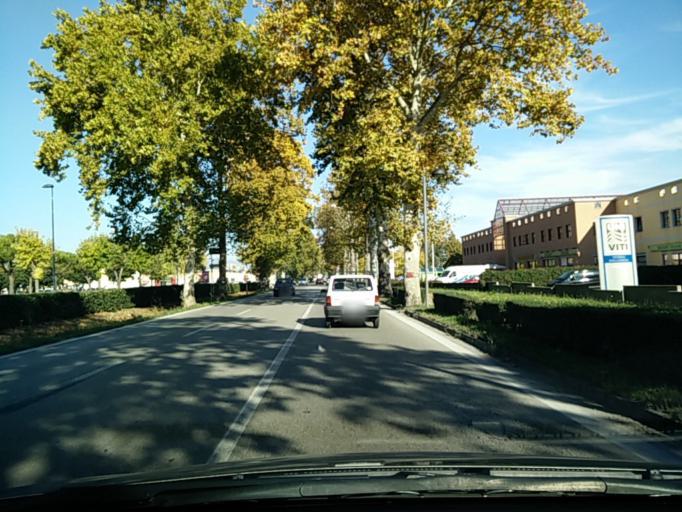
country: IT
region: Veneto
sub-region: Provincia di Treviso
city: Spresiano
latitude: 45.7704
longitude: 12.2534
